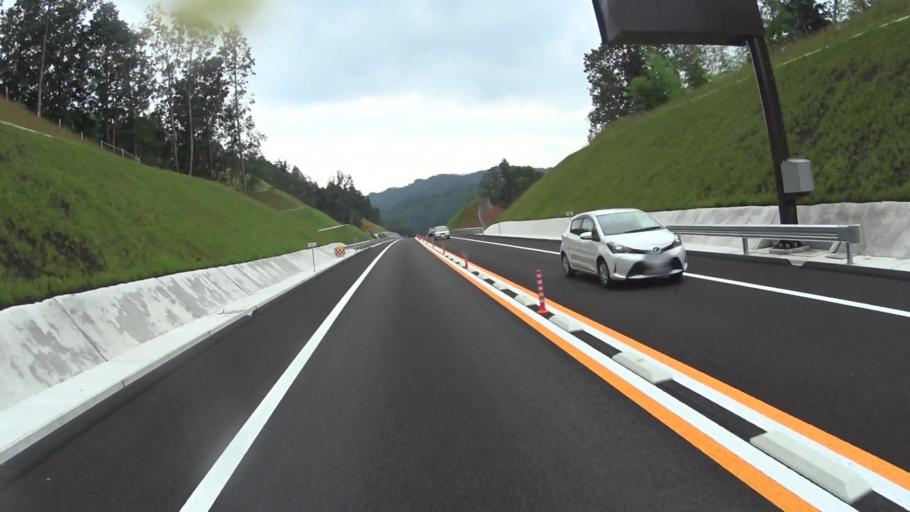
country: JP
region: Kyoto
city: Ayabe
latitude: 35.2262
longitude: 135.3447
